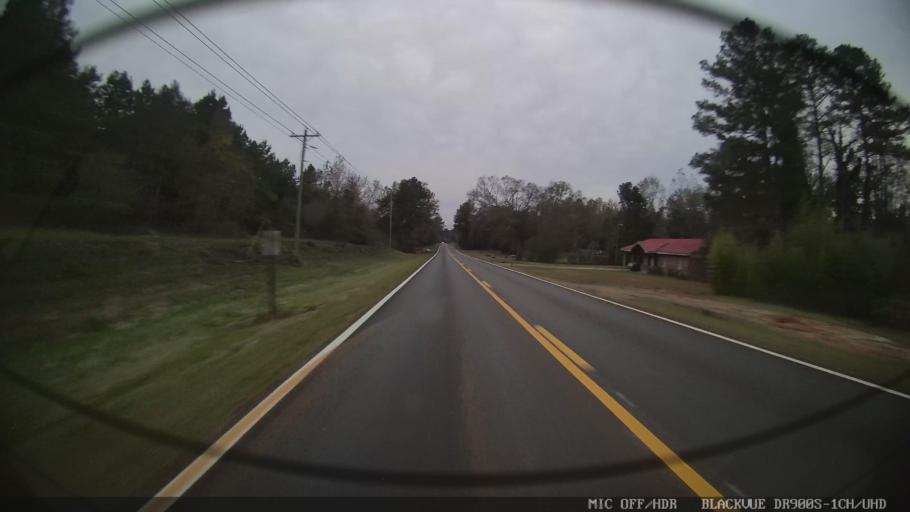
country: US
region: Mississippi
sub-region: Clarke County
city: Quitman
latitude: 32.0505
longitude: -88.6915
